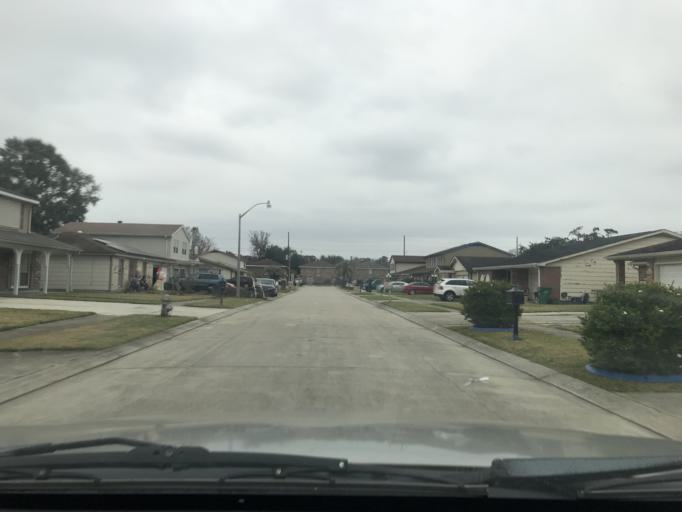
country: US
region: Louisiana
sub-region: Jefferson Parish
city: Woodmere
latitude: 29.8614
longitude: -90.0764
